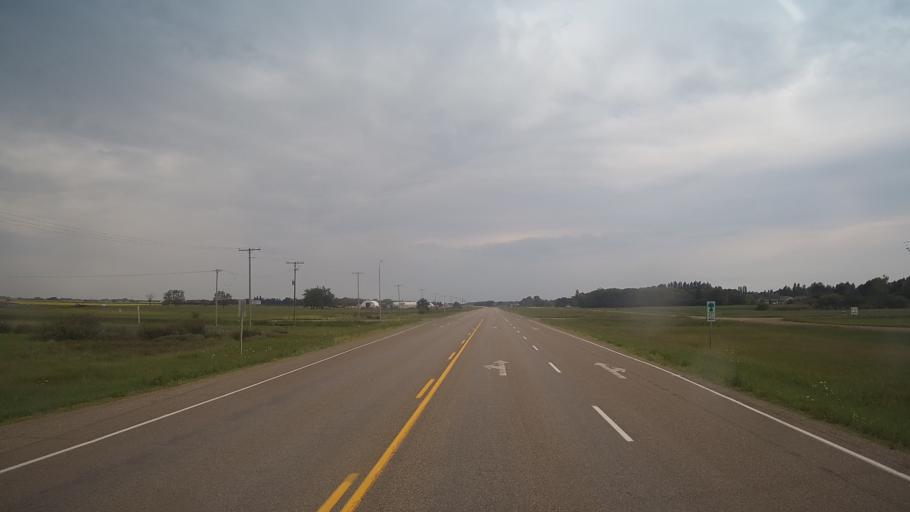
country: CA
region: Saskatchewan
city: Langham
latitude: 52.1289
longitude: -107.2155
